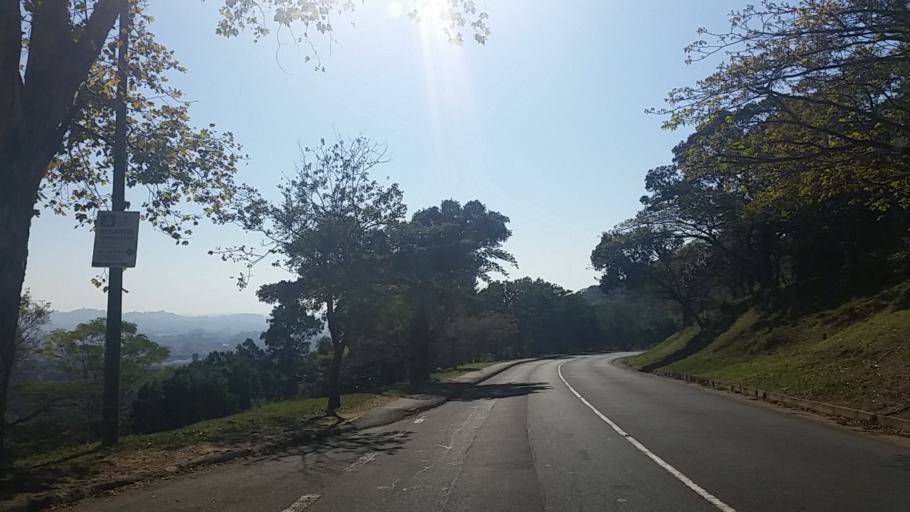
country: ZA
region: KwaZulu-Natal
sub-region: eThekwini Metropolitan Municipality
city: Berea
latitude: -29.8284
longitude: 30.8853
